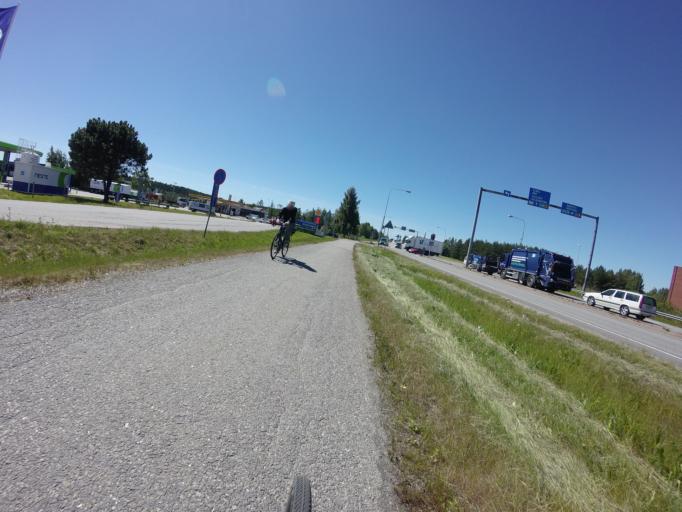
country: FI
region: Varsinais-Suomi
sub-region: Turku
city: Turku
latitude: 60.4878
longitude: 22.3240
